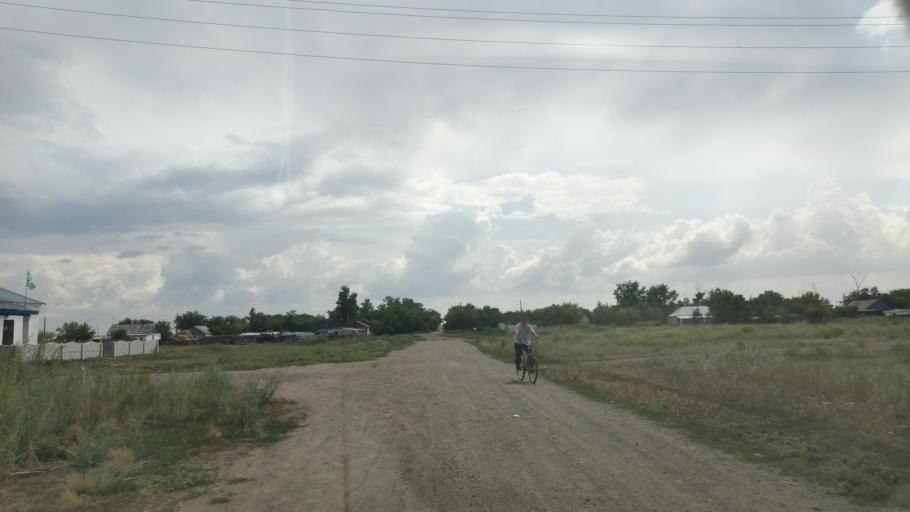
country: KZ
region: Pavlodar
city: Pavlodar
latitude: 52.6196
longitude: 77.2067
